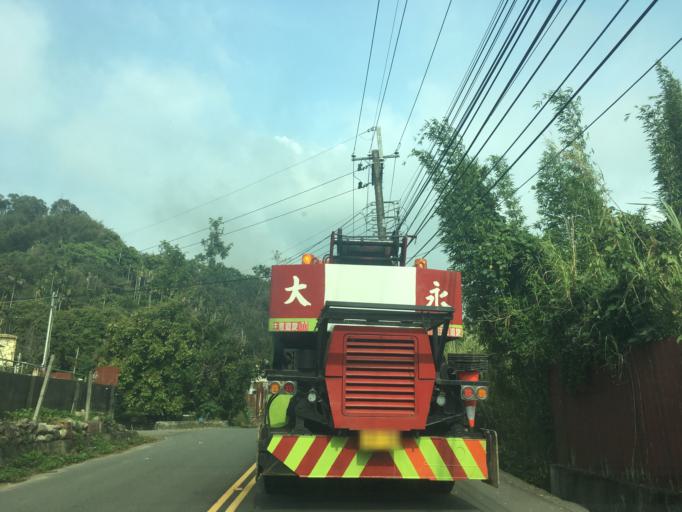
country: TW
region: Taiwan
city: Fengyuan
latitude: 24.2346
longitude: 120.7449
